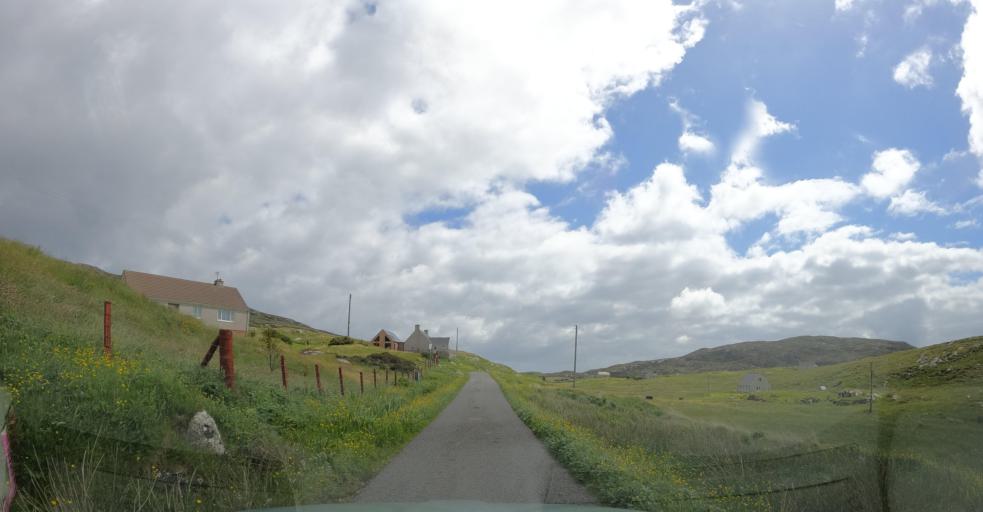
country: GB
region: Scotland
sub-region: Eilean Siar
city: Isle of South Uist
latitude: 57.0716
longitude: -7.2972
